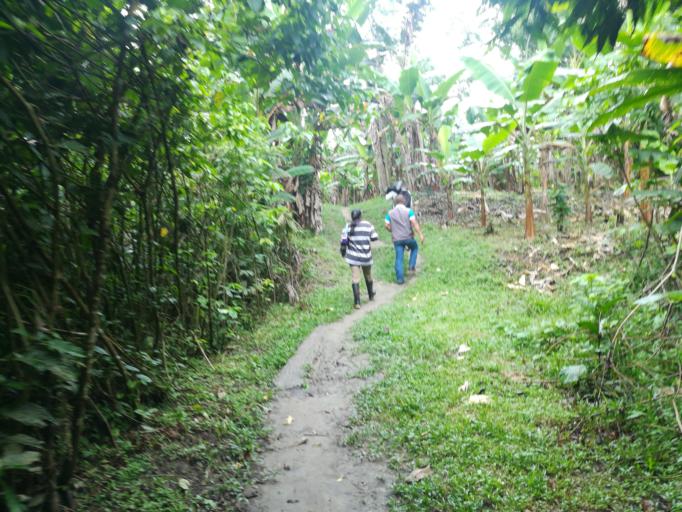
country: EC
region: Orellana
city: Boca Suno
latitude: -0.7515
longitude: -77.1534
